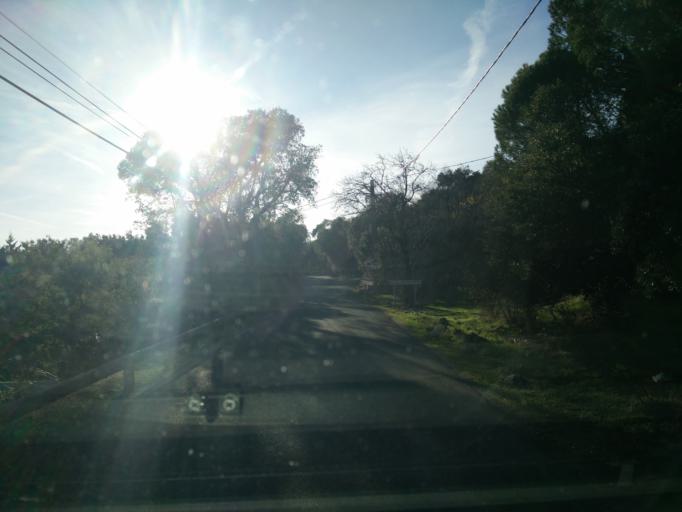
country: FR
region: Provence-Alpes-Cote d'Azur
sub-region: Departement du Var
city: Le Plan-de-la-Tour
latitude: 43.3394
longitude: 6.5441
